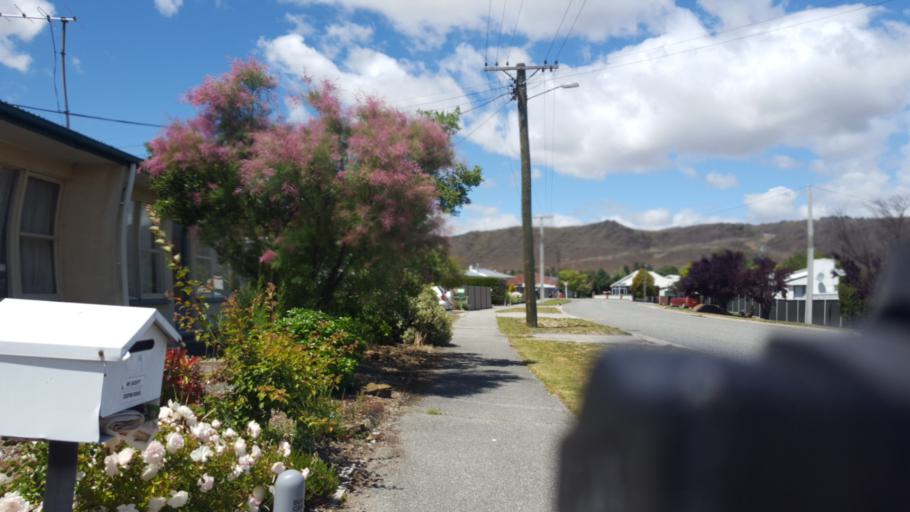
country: NZ
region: Otago
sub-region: Queenstown-Lakes District
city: Wanaka
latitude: -45.2479
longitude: 169.3934
